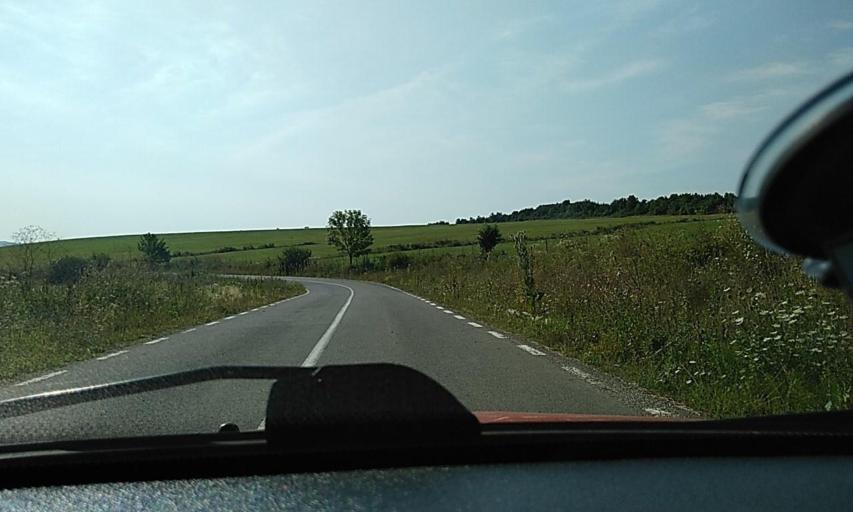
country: RO
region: Brasov
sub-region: Comuna Bunesti
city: Bunesti
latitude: 46.0634
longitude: 25.0802
